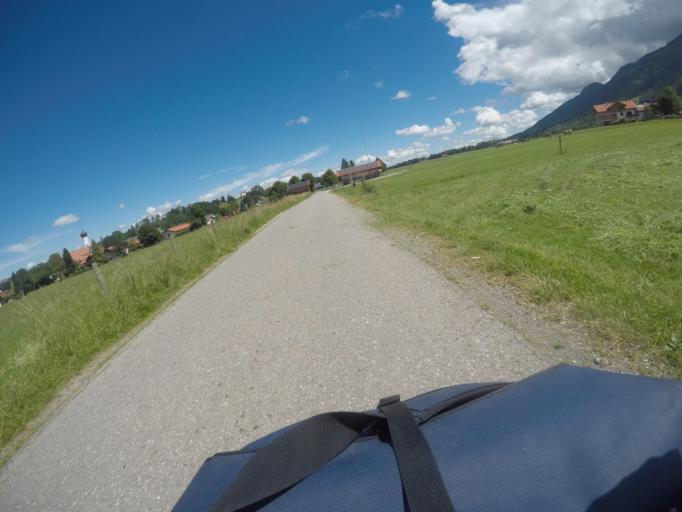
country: DE
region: Bavaria
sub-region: Swabia
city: Halblech
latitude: 47.6222
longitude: 10.8025
